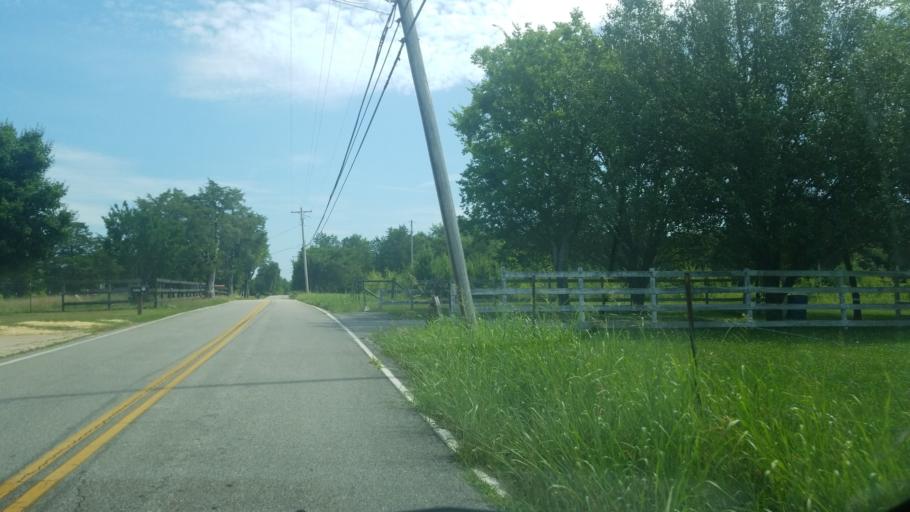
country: US
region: Tennessee
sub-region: Hamilton County
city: Lakesite
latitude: 35.2043
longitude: -85.0251
